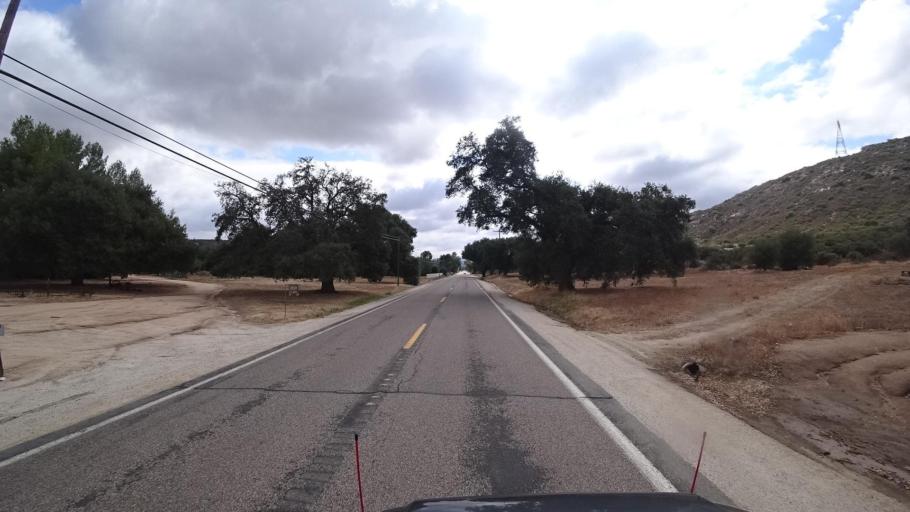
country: US
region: California
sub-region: San Diego County
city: Campo
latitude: 32.6646
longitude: -116.4881
